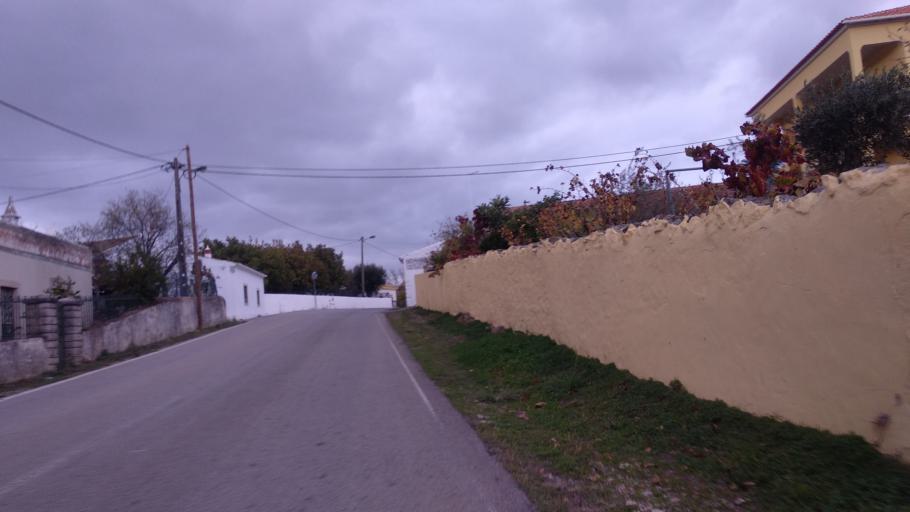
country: PT
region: Faro
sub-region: Sao Bras de Alportel
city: Sao Bras de Alportel
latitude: 37.1699
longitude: -7.9079
